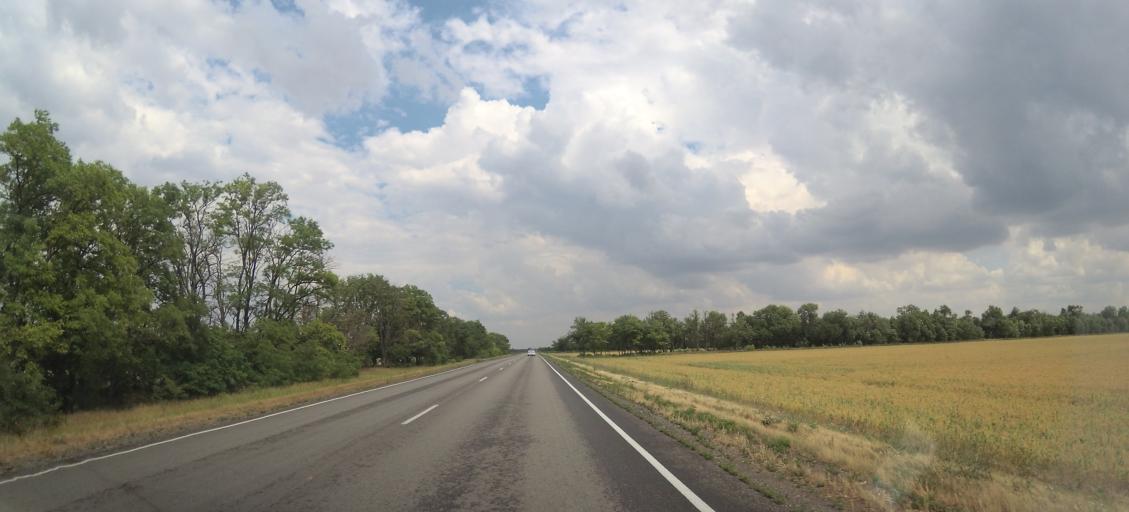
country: RU
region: Rostov
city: Letnik
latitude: 46.0869
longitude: 41.1686
